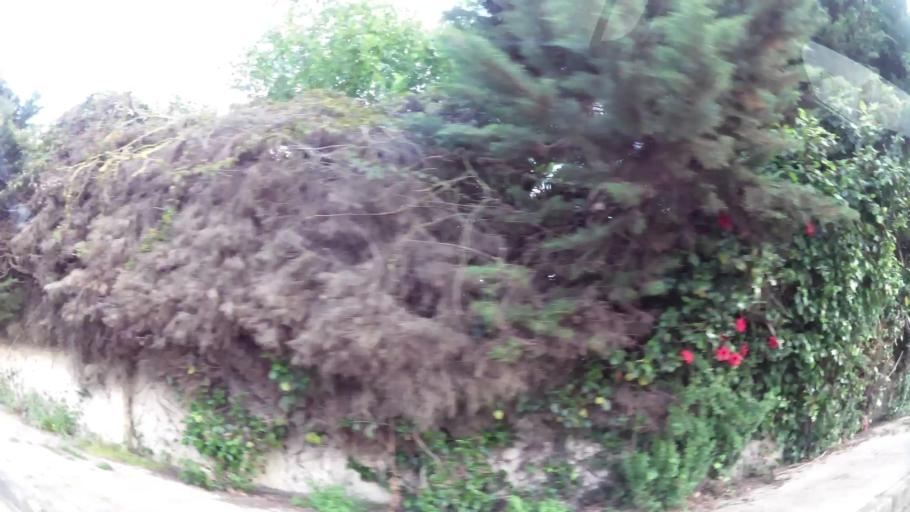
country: MA
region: Rabat-Sale-Zemmour-Zaer
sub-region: Rabat
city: Rabat
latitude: 33.9550
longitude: -6.8355
